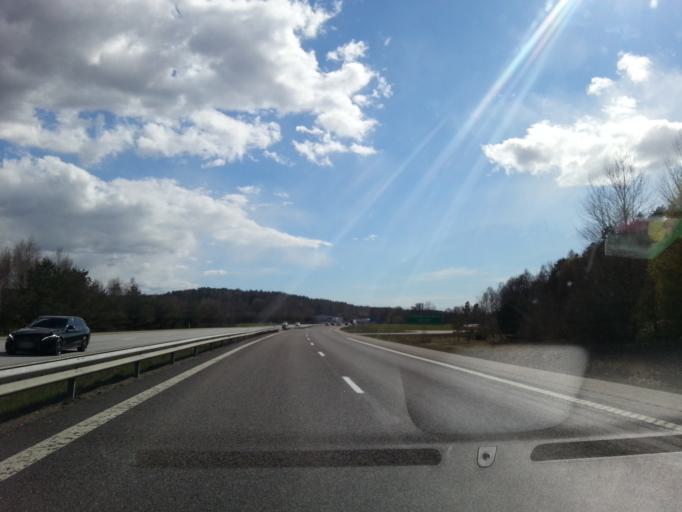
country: SE
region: Vaestra Goetaland
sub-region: Stenungsunds Kommun
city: Stenungsund
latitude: 58.0681
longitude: 11.8903
